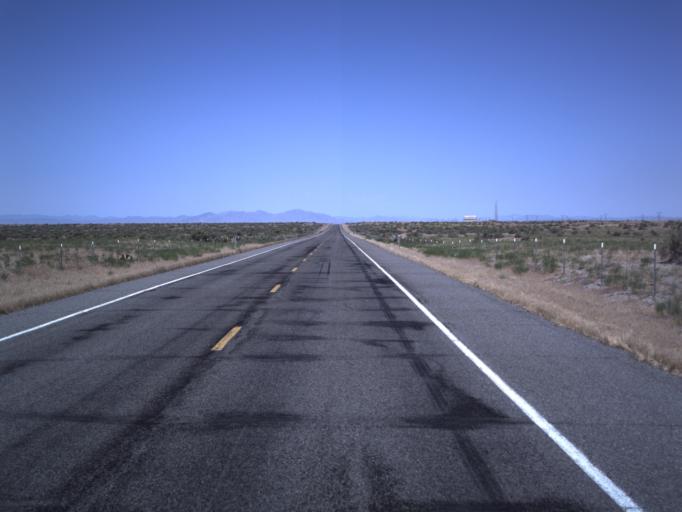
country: US
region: Utah
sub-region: Millard County
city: Delta
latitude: 39.4733
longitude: -112.4753
